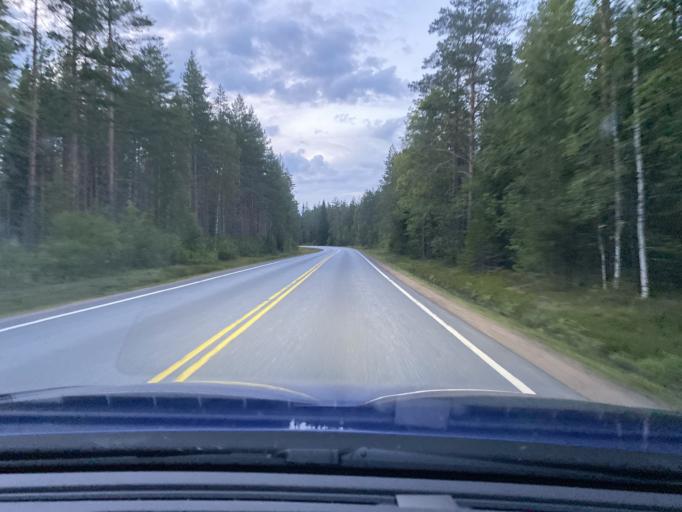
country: FI
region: Southern Ostrobothnia
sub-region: Suupohja
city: Kauhajoki
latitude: 62.2453
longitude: 22.2725
